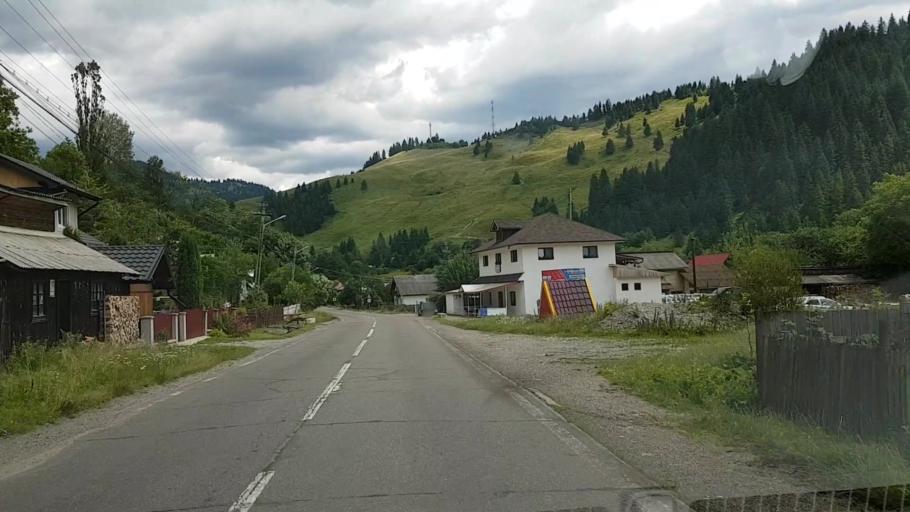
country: RO
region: Suceava
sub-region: Comuna Brosteni
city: Brosteni
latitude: 47.2332
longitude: 25.7206
